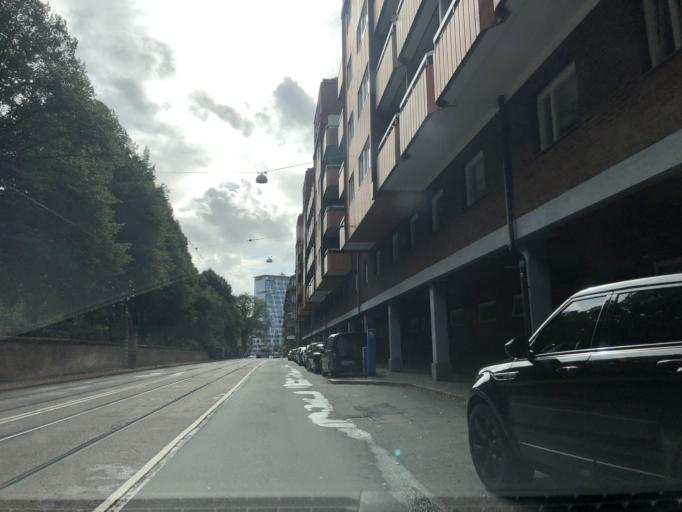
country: SE
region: Vaestra Goetaland
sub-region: Goteborg
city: Goeteborg
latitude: 57.7099
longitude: 11.9878
